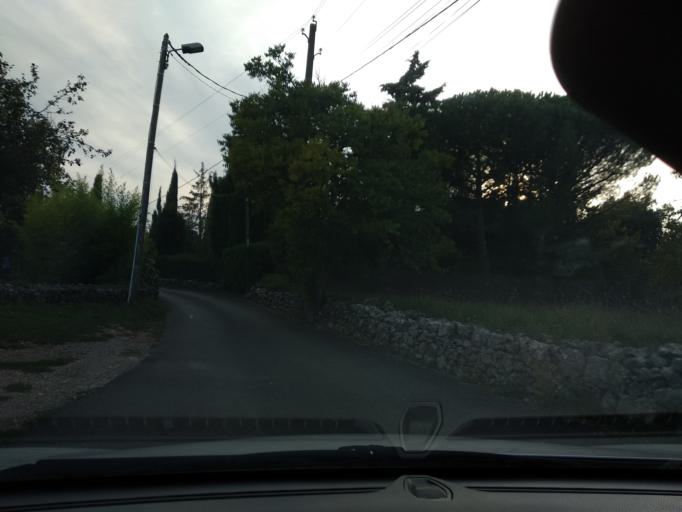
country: FR
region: Provence-Alpes-Cote d'Azur
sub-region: Departement des Alpes-Maritimes
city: Saint-Cezaire-sur-Siagne
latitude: 43.6568
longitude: 6.8026
